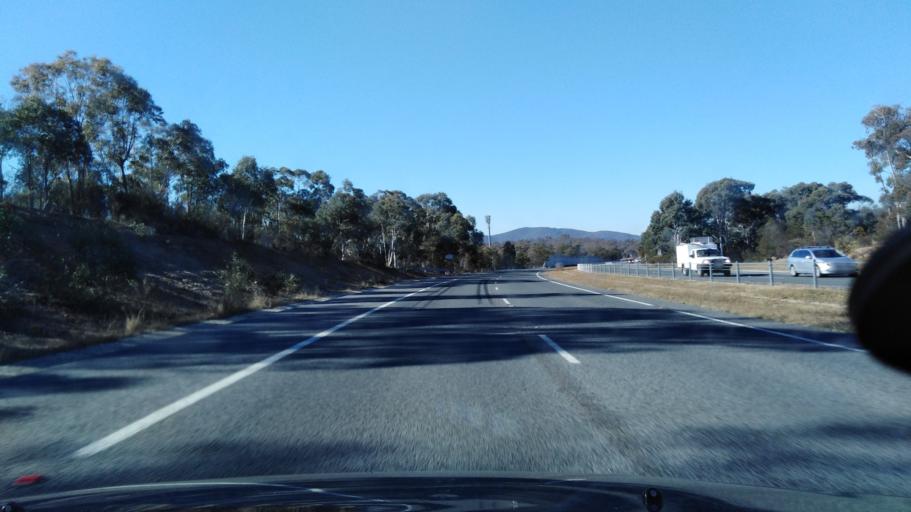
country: AU
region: Australian Capital Territory
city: Macquarie
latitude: -35.2523
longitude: 149.0967
